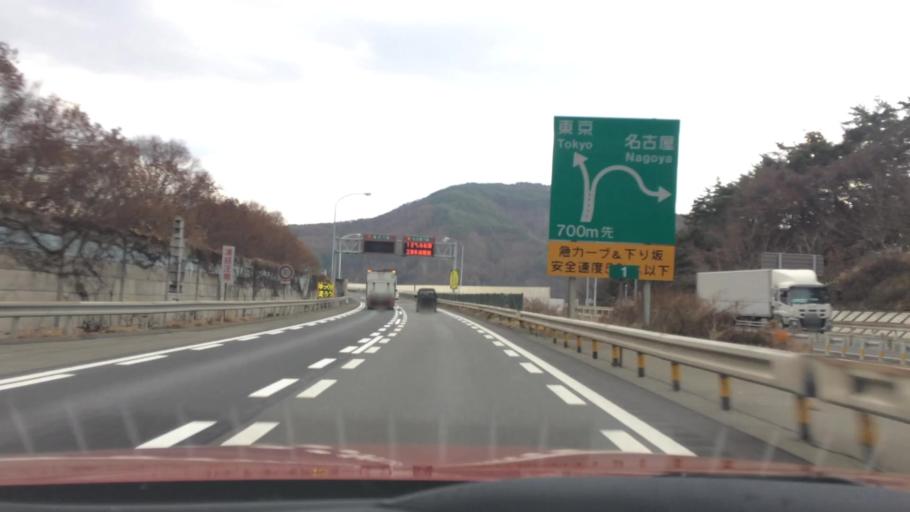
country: JP
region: Nagano
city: Okaya
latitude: 36.0594
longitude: 138.0372
